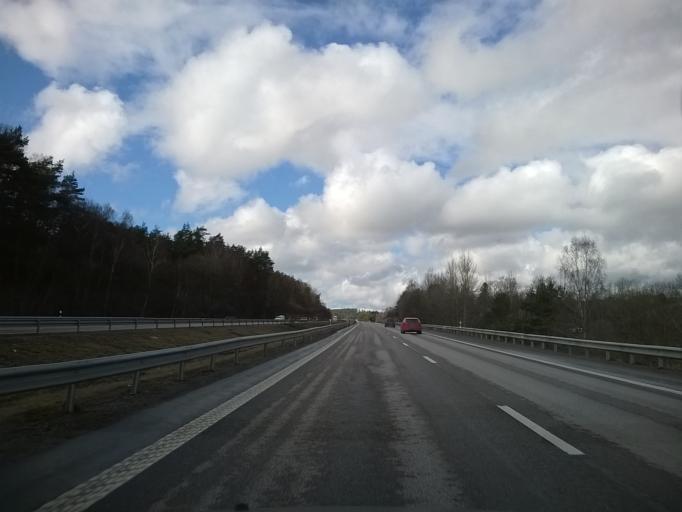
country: SE
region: Halland
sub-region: Kungsbacka Kommun
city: Frillesas
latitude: 57.3733
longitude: 12.2007
